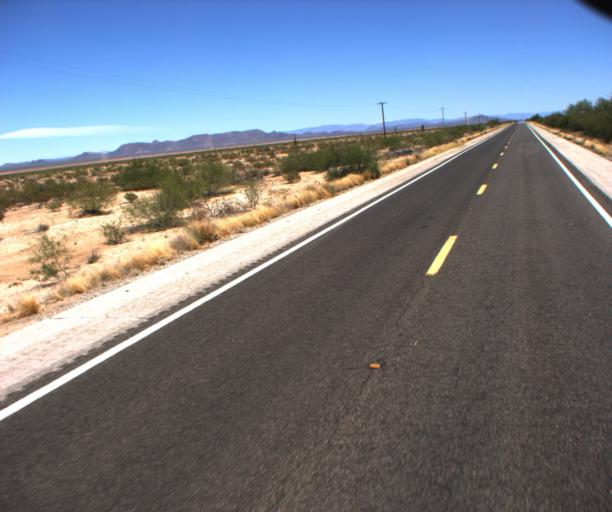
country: US
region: Arizona
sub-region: La Paz County
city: Salome
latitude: 33.9169
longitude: -113.2582
